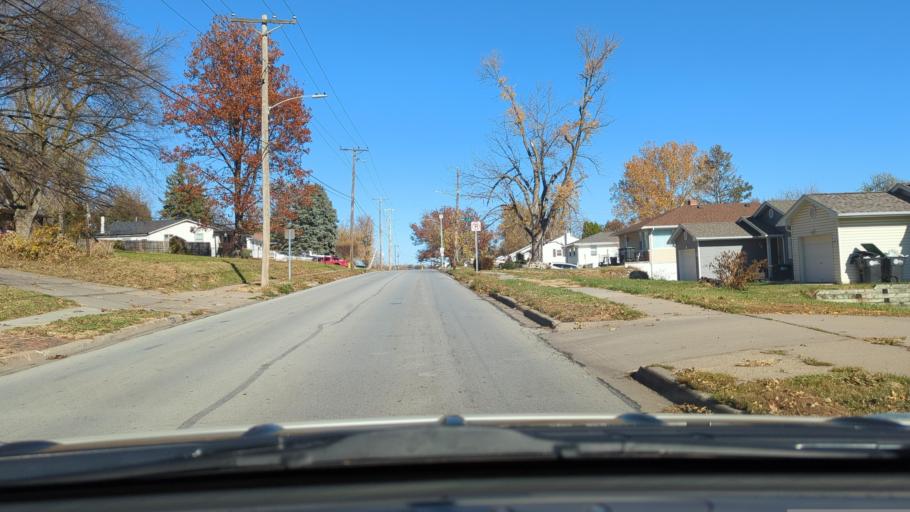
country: US
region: Nebraska
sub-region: Sarpy County
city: La Vista
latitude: 41.1956
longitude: -95.9770
